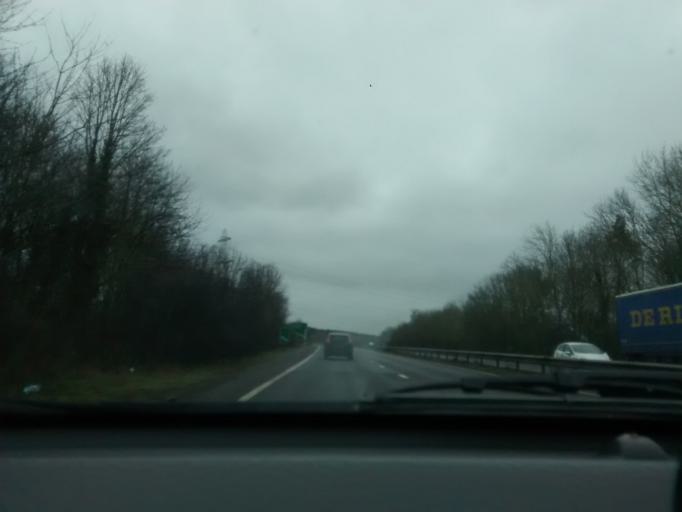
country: GB
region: England
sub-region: Suffolk
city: Needham Market
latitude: 52.1511
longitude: 1.0727
